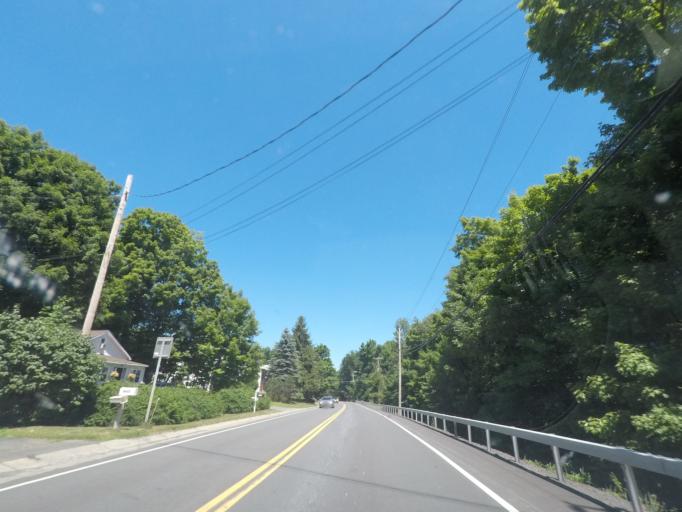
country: US
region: New York
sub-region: Rensselaer County
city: West Sand Lake
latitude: 42.6499
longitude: -73.6102
